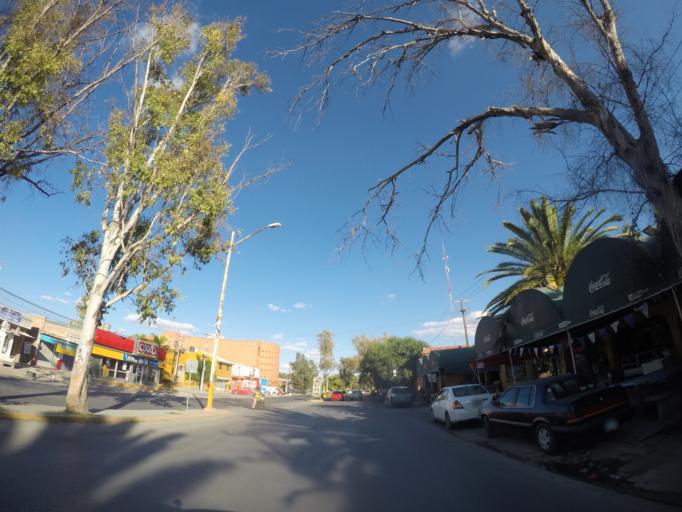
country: MX
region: San Luis Potosi
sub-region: San Luis Potosi
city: San Luis Potosi
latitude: 22.1823
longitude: -100.9996
